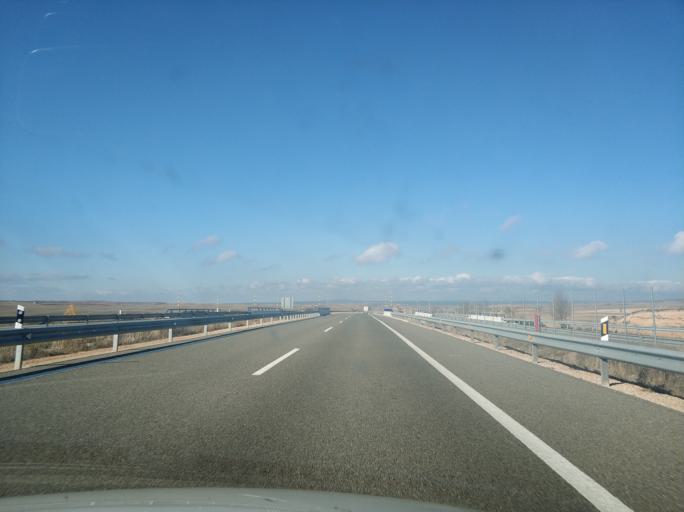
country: ES
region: Castille and Leon
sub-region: Provincia de Soria
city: Coscurita
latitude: 41.3950
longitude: -2.4737
